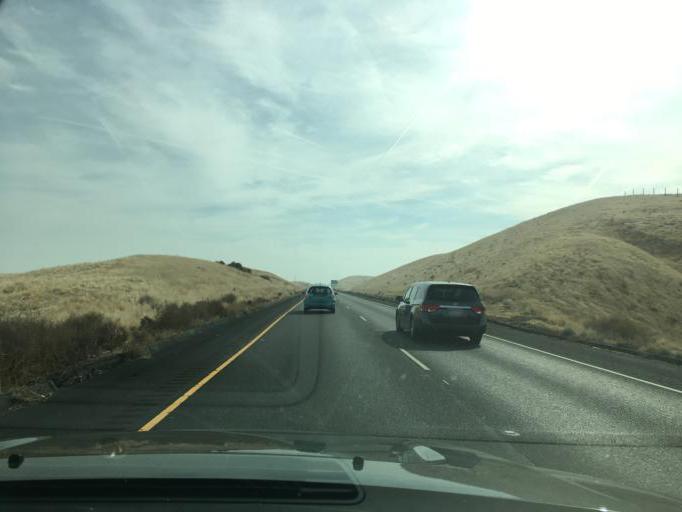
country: US
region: California
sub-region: Kings County
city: Kettleman City
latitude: 36.0031
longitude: -119.9823
